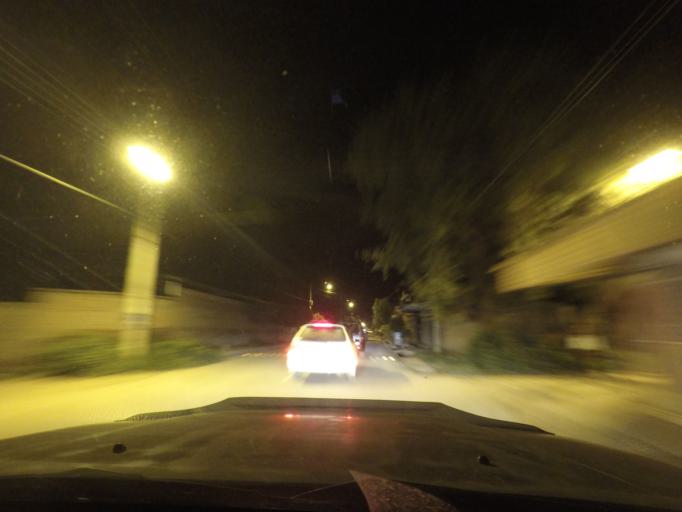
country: BO
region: Cochabamba
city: Cochabamba
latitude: -17.3773
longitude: -66.2023
